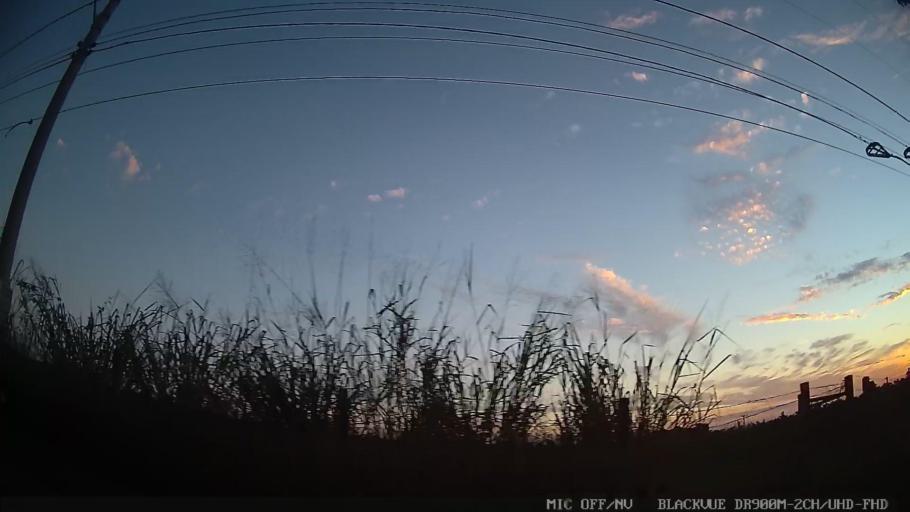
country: BR
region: Sao Paulo
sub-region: Indaiatuba
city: Indaiatuba
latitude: -23.1427
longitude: -47.1598
